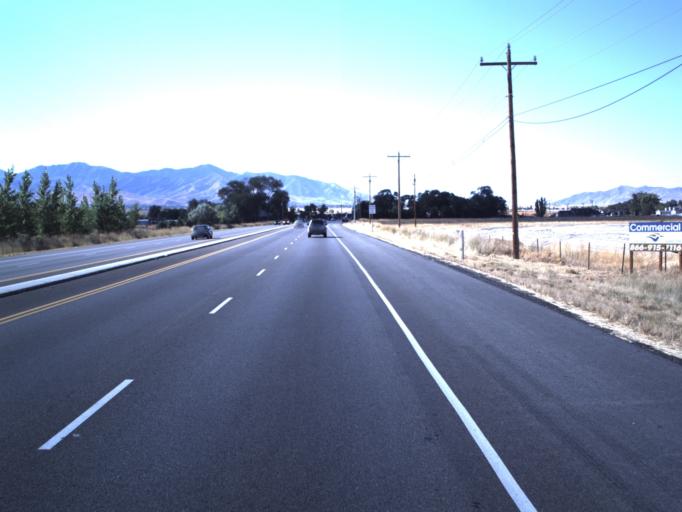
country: US
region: Utah
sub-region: Tooele County
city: Erda
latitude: 40.6215
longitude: -112.2938
